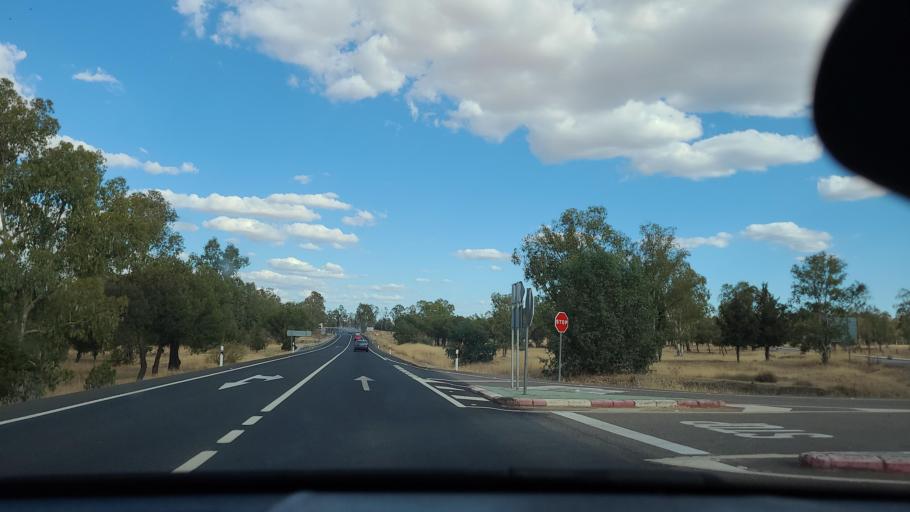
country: ES
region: Extremadura
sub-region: Provincia de Badajoz
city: Berlanga
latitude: 38.2735
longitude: -5.8157
